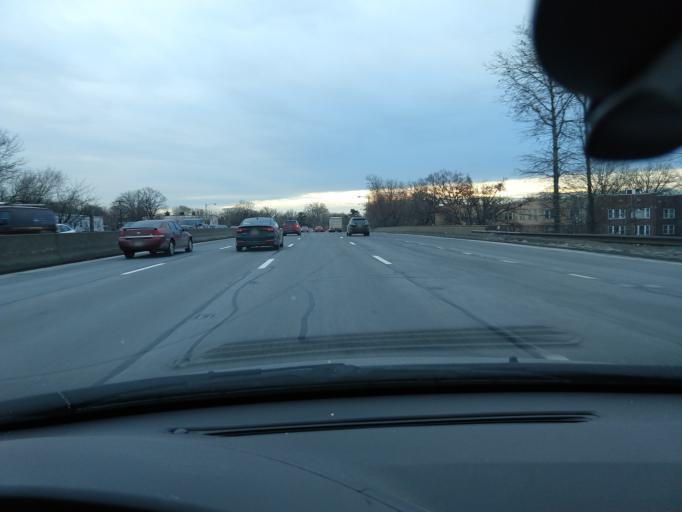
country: US
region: New Jersey
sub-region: Essex County
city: Irvington
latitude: 40.7219
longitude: -74.2317
